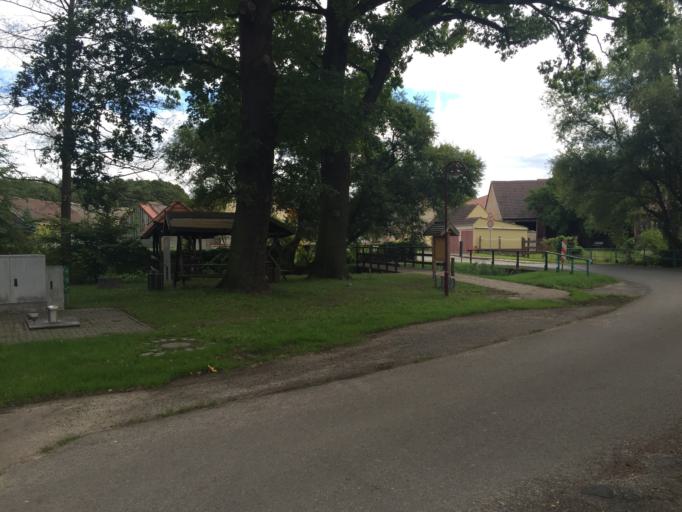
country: DE
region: Brandenburg
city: Belzig
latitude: 52.1734
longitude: 12.6765
